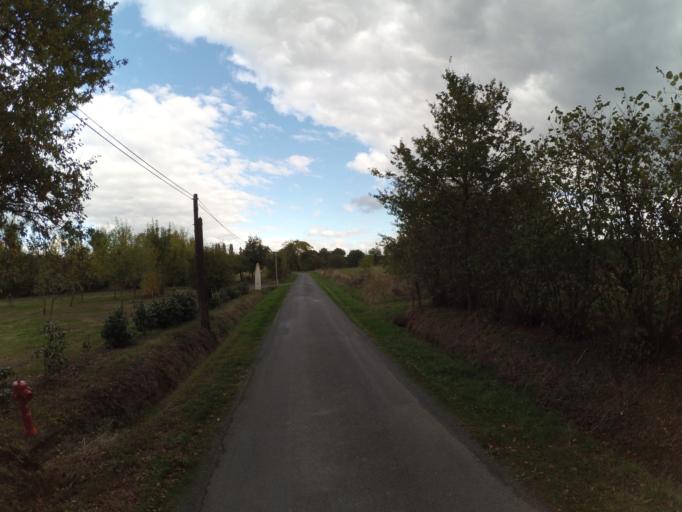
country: FR
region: Pays de la Loire
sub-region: Departement de la Loire-Atlantique
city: Remouille
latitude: 47.0625
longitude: -1.3701
